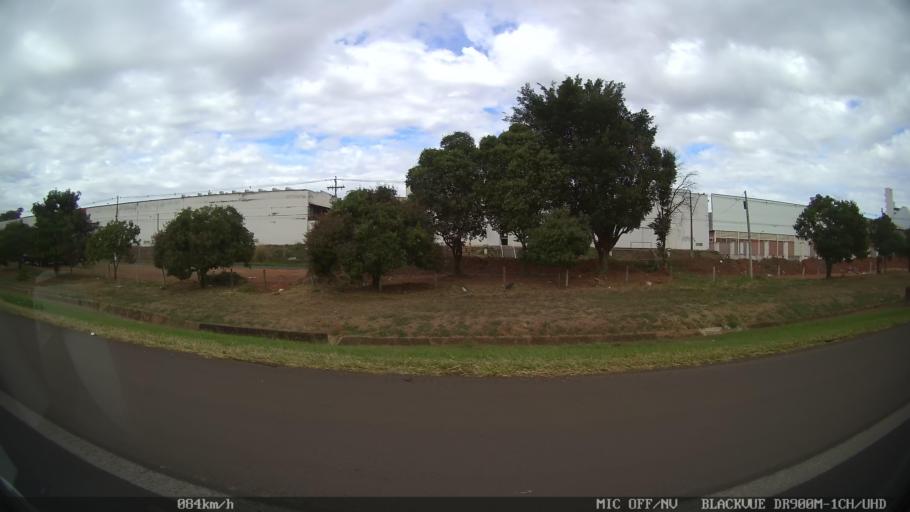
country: BR
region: Sao Paulo
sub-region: Bady Bassitt
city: Bady Bassitt
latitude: -20.8067
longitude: -49.5149
